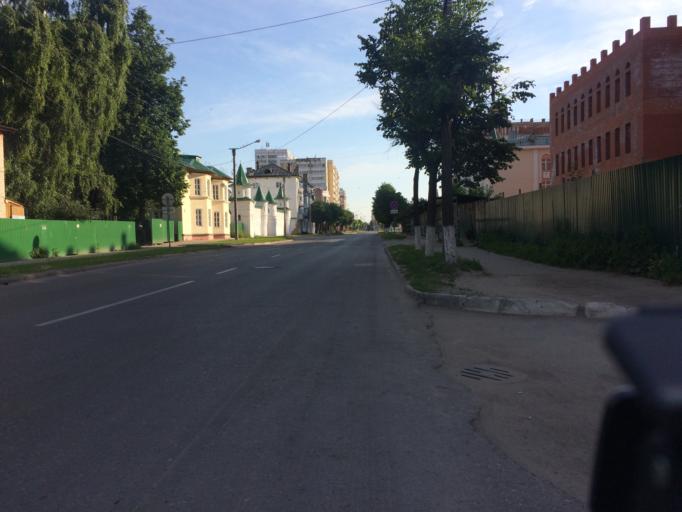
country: RU
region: Mariy-El
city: Yoshkar-Ola
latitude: 56.6325
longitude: 47.8984
